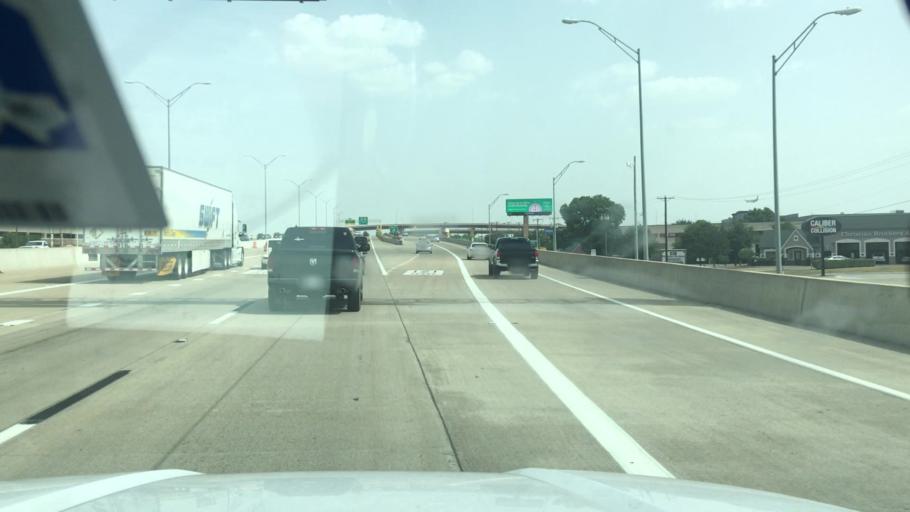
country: US
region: Texas
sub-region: Tarrant County
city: Grapevine
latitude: 32.9357
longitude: -97.0980
